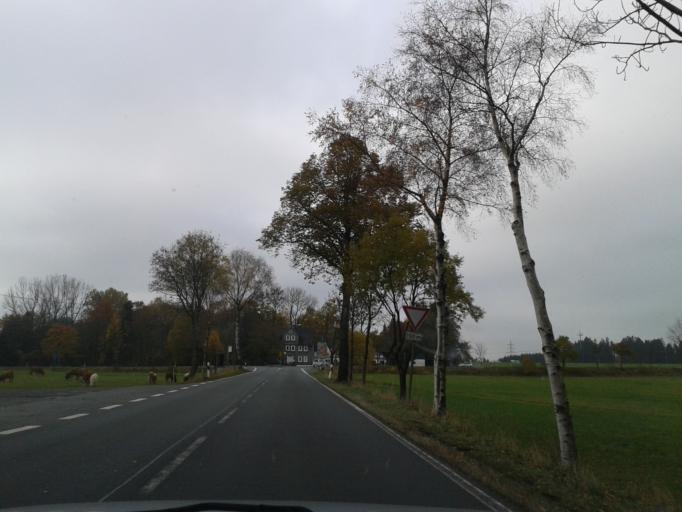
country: DE
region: North Rhine-Westphalia
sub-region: Regierungsbezirk Arnsberg
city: Erndtebruck
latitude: 50.9836
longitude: 8.3305
